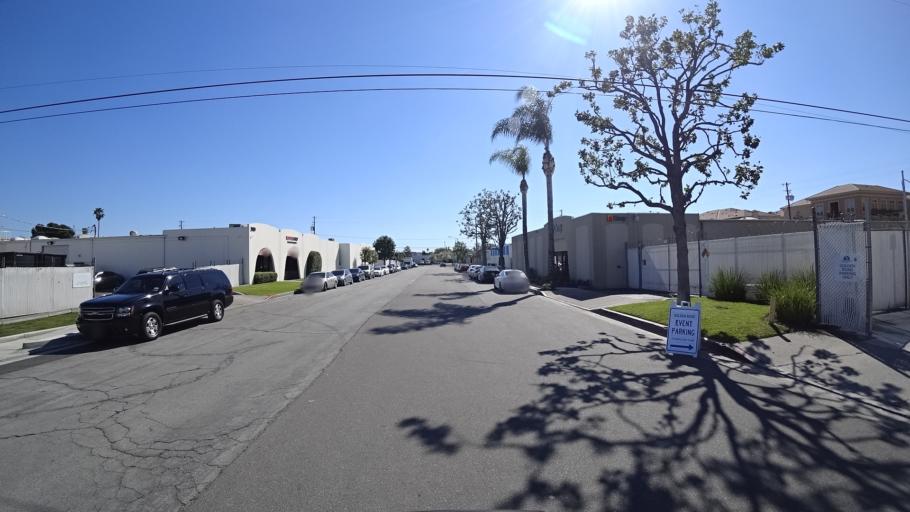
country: US
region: California
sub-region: Orange County
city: Orange
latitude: 33.7953
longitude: -117.8858
